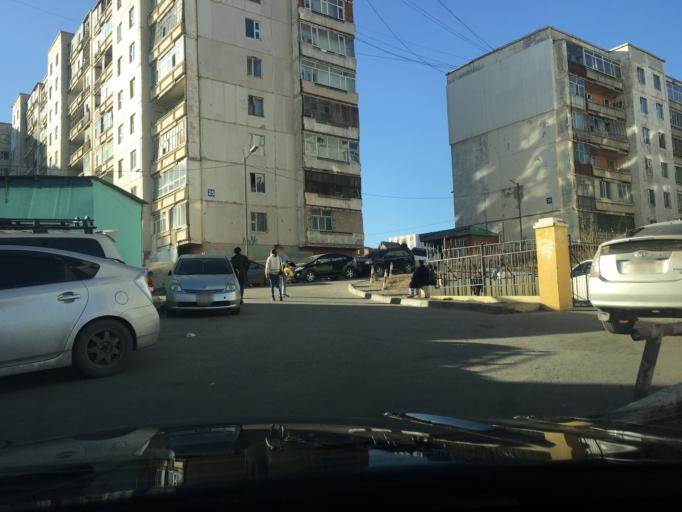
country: MN
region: Ulaanbaatar
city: Ulaanbaatar
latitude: 47.9278
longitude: 106.8815
